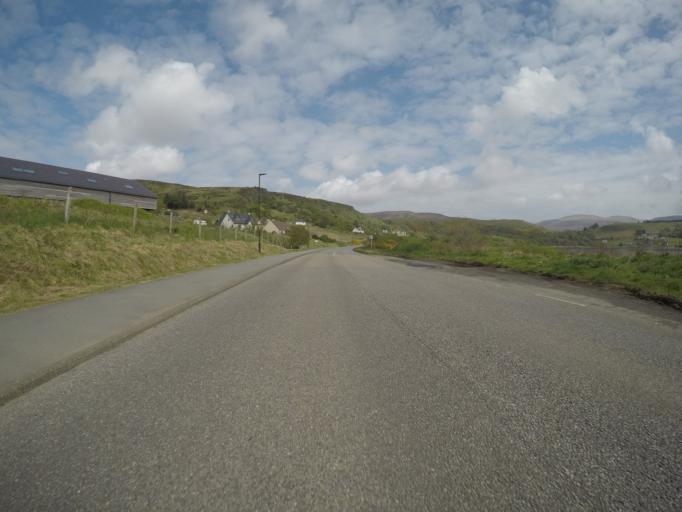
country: GB
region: Scotland
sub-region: Highland
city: Portree
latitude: 57.5897
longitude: -6.3730
